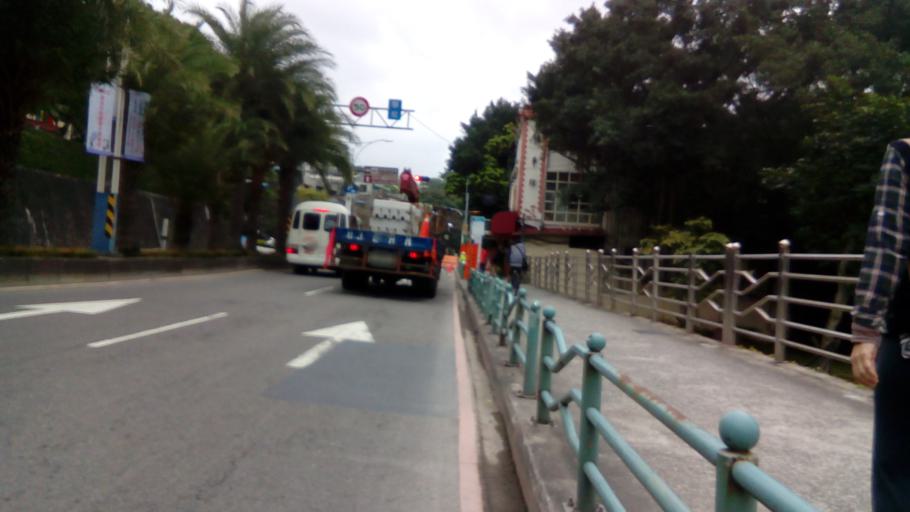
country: TW
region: Taipei
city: Taipei
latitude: 25.1745
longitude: 121.4328
